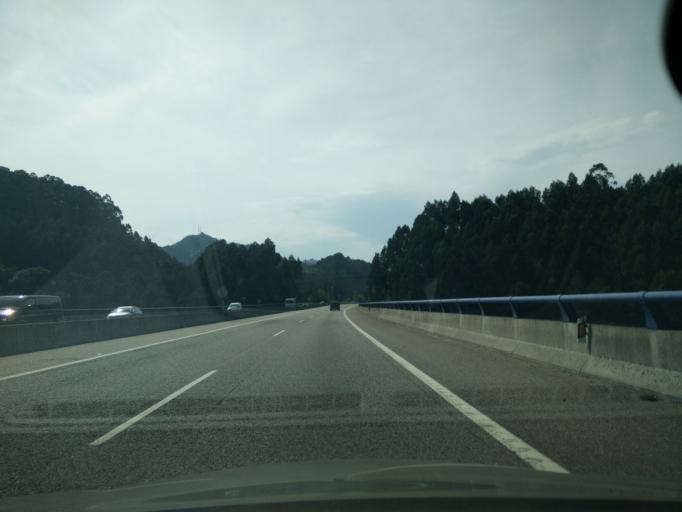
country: ES
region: Asturias
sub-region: Province of Asturias
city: Ribadesella
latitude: 43.4350
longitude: -5.0608
